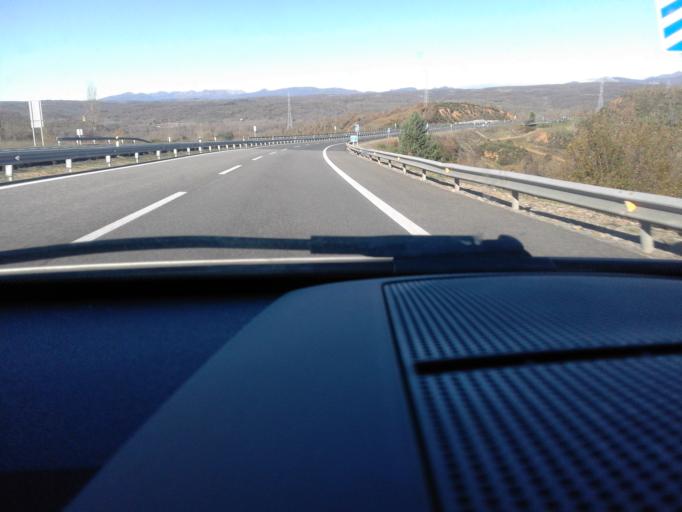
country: ES
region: Castille and Leon
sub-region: Provincia de Leon
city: Santa Maria de Ordas
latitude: 42.7082
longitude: -5.7939
